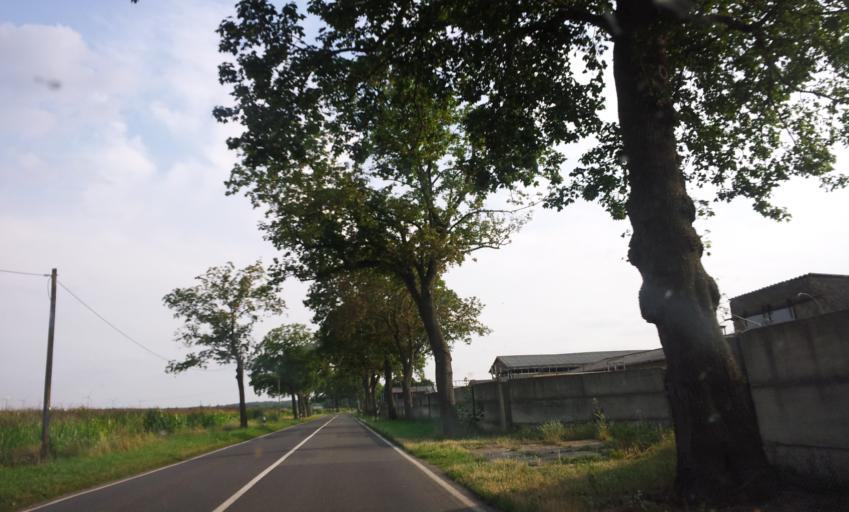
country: DE
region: Brandenburg
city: Treuenbrietzen
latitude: 52.0858
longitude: 12.9454
